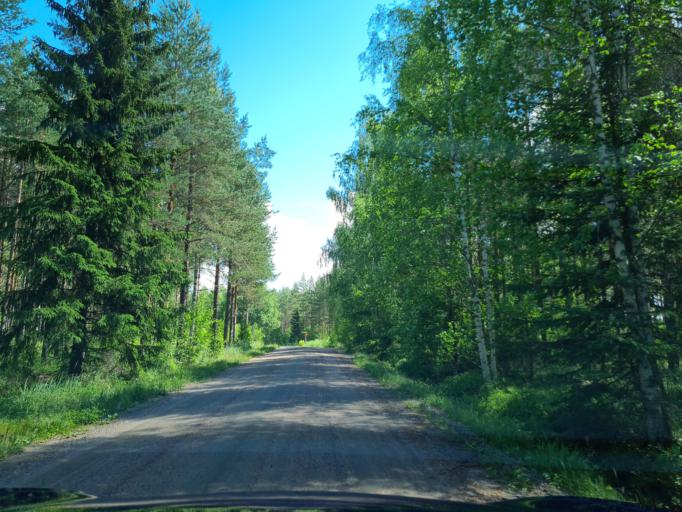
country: FI
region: Uusimaa
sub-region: Helsinki
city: Kaerkoelae
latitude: 60.7544
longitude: 23.9581
